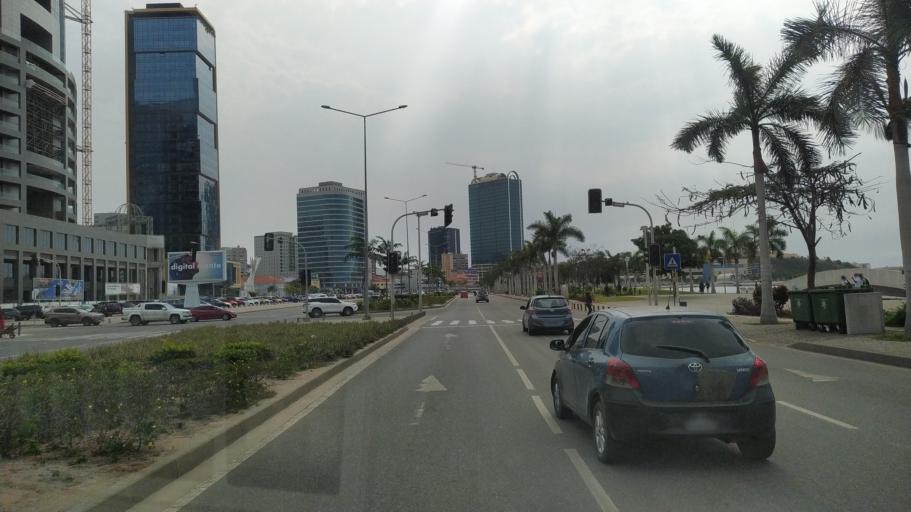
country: AO
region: Luanda
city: Luanda
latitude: -8.8101
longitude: 13.2336
